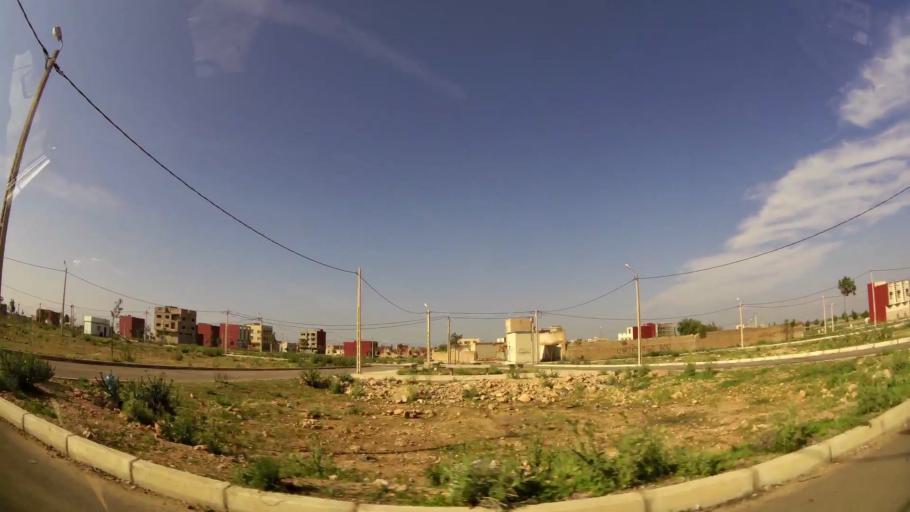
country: MA
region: Oriental
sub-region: Oujda-Angad
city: Oujda
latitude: 34.7158
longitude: -1.8864
